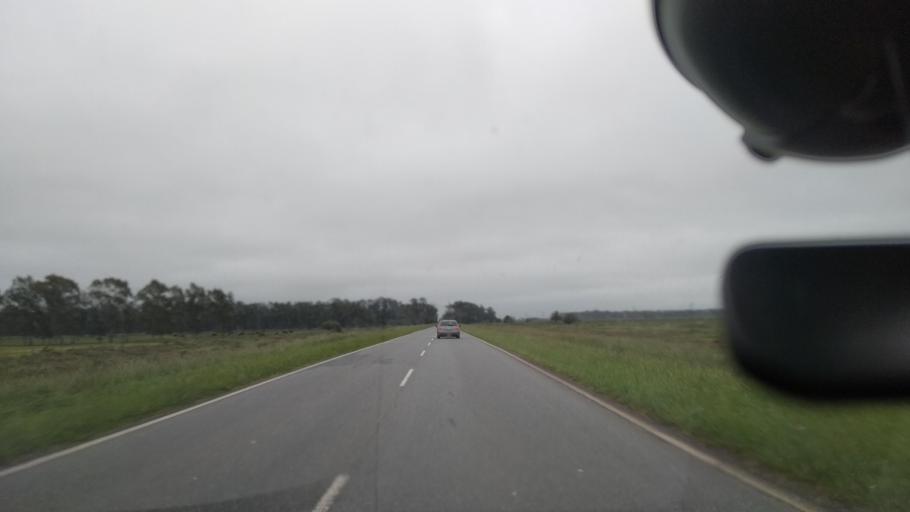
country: AR
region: Buenos Aires
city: Veronica
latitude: -35.3232
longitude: -57.4739
